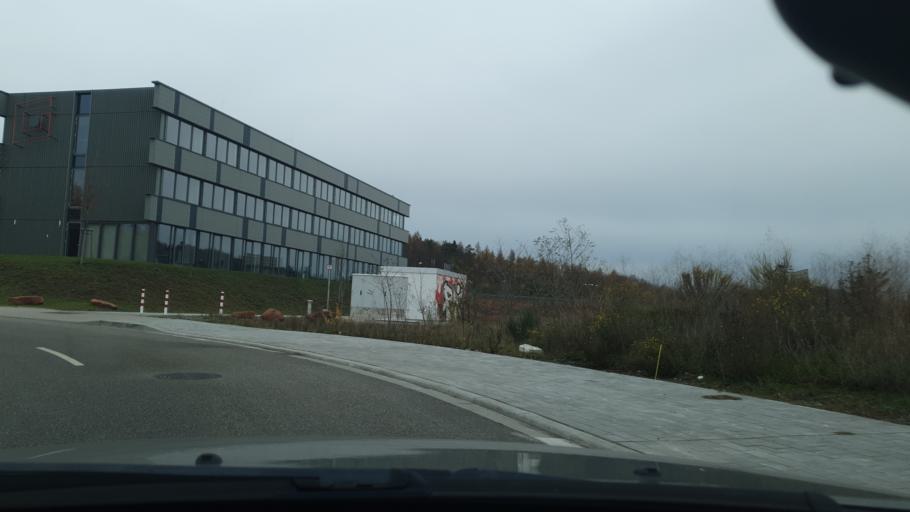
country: DE
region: Rheinland-Pfalz
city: Kaiserslautern
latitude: 49.4527
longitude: 7.8161
